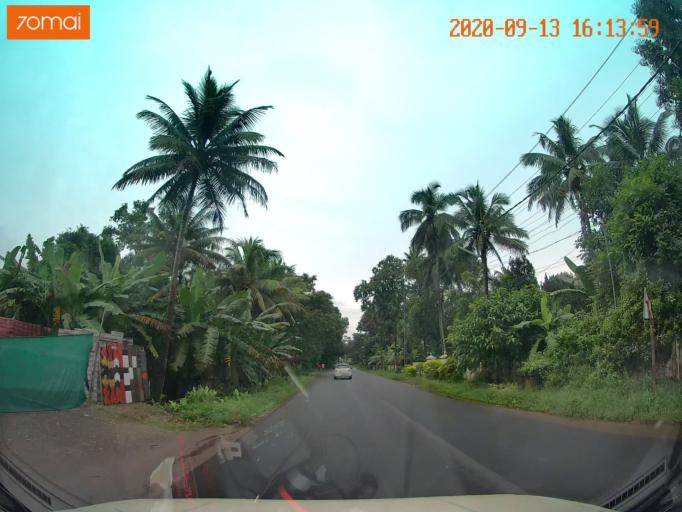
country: IN
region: Kerala
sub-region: Kottayam
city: Palackattumala
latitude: 9.6886
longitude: 76.6311
